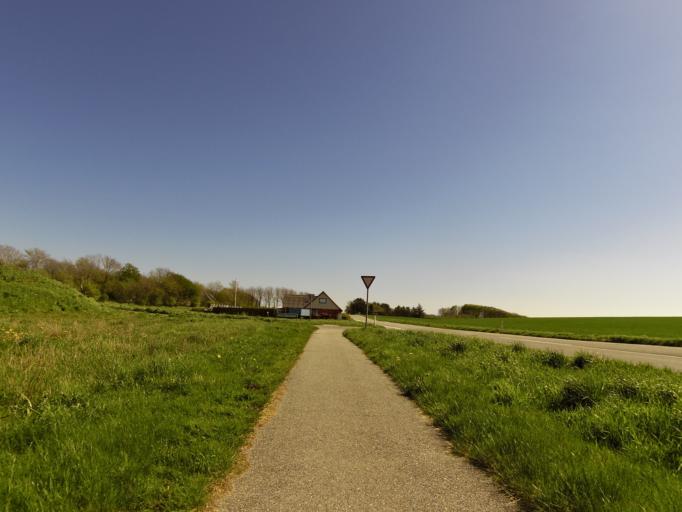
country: DK
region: Central Jutland
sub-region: Holstebro Kommune
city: Vinderup
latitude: 56.5976
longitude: 8.7744
